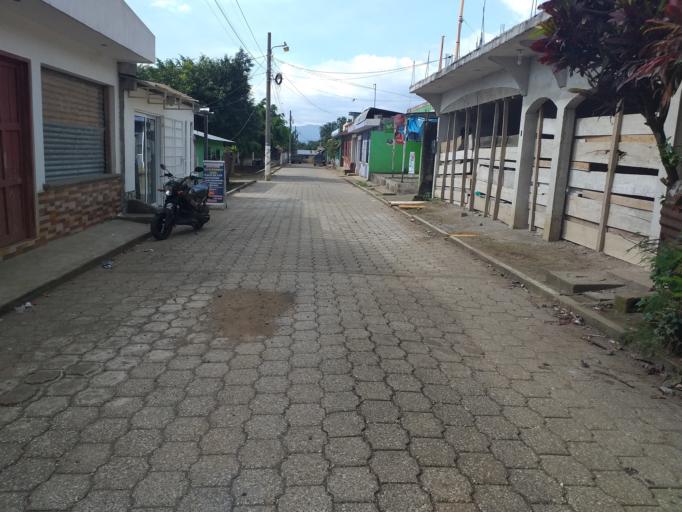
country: GT
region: Suchitepeque
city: Pueblo Nuevo
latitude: 14.6483
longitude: -91.5545
